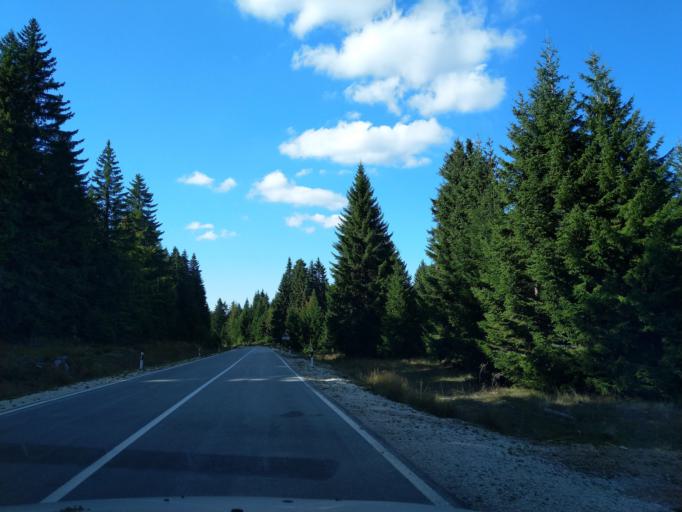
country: RS
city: Sokolovica
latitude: 43.2837
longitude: 20.3255
